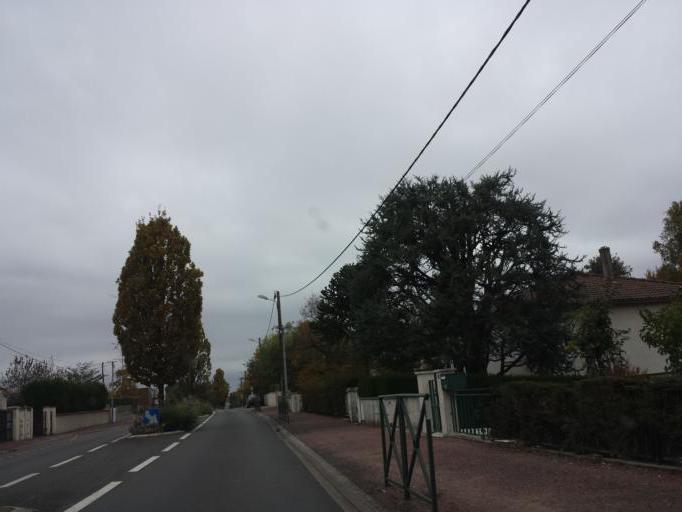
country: FR
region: Poitou-Charentes
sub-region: Departement de la Charente
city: Puymoyen
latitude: 45.6170
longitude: 0.1752
